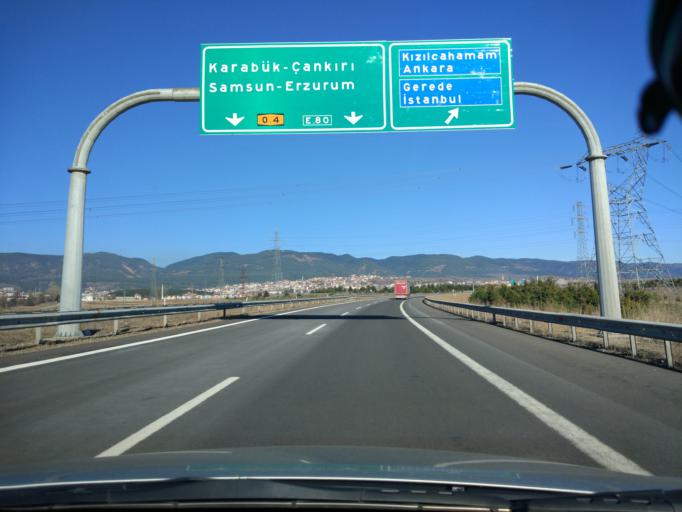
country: TR
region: Bolu
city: Gerede
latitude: 40.7751
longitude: 32.2054
